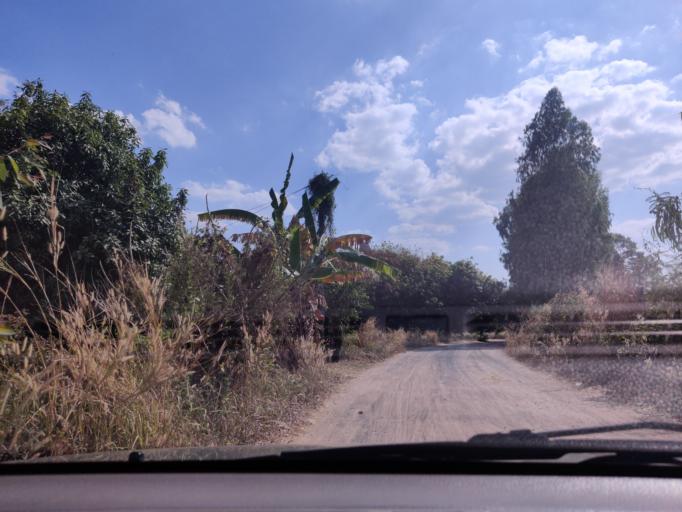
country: TH
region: Sisaket
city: Si Sa Ket
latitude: 15.0799
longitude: 104.3508
